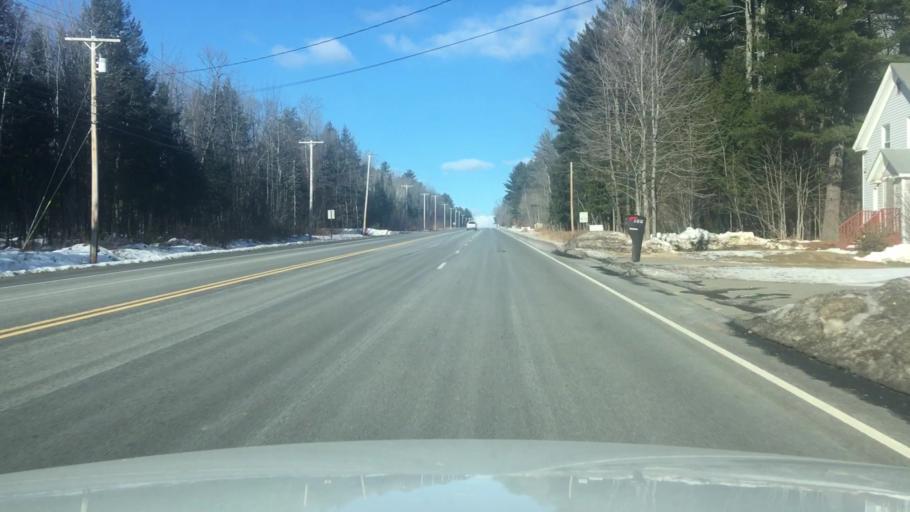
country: US
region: Maine
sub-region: Somerset County
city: Skowhegan
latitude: 44.7965
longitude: -69.7487
